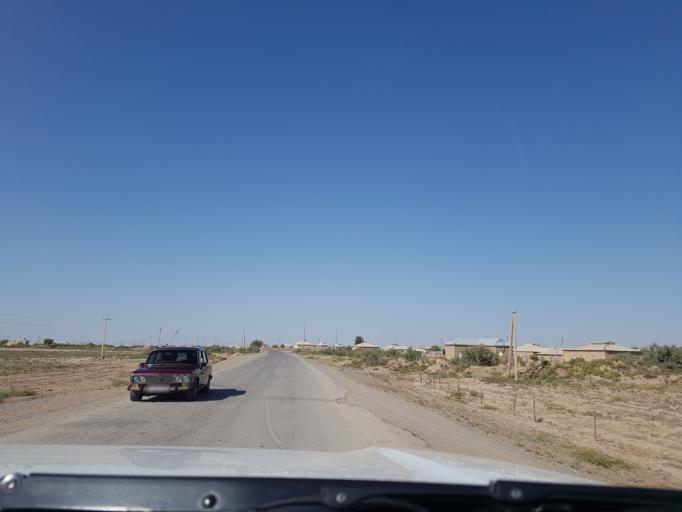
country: IR
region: Razavi Khorasan
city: Sarakhs
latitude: 36.5124
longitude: 61.2532
